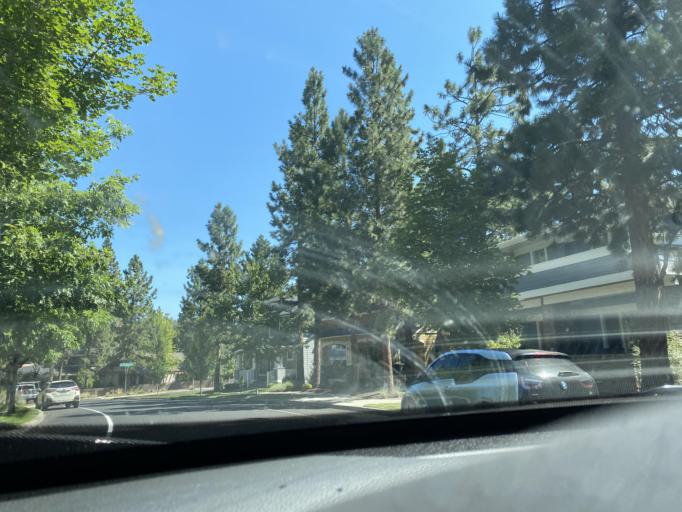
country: US
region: Oregon
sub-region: Deschutes County
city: Bend
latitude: 44.0584
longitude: -121.3503
